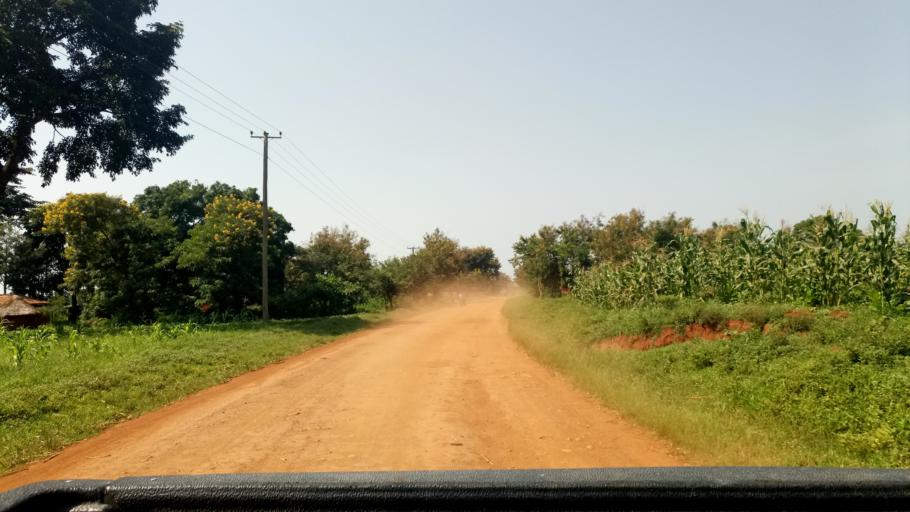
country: UG
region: Eastern Region
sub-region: Kaliro District
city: Kaliro
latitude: 0.9622
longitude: 33.4699
